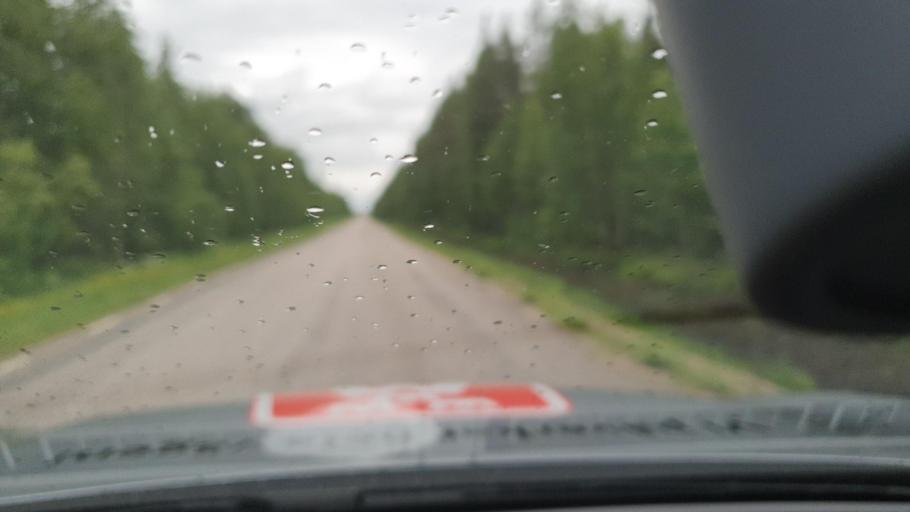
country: SE
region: Norrbotten
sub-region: Overkalix Kommun
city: OEverkalix
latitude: 66.3686
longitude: 22.8013
